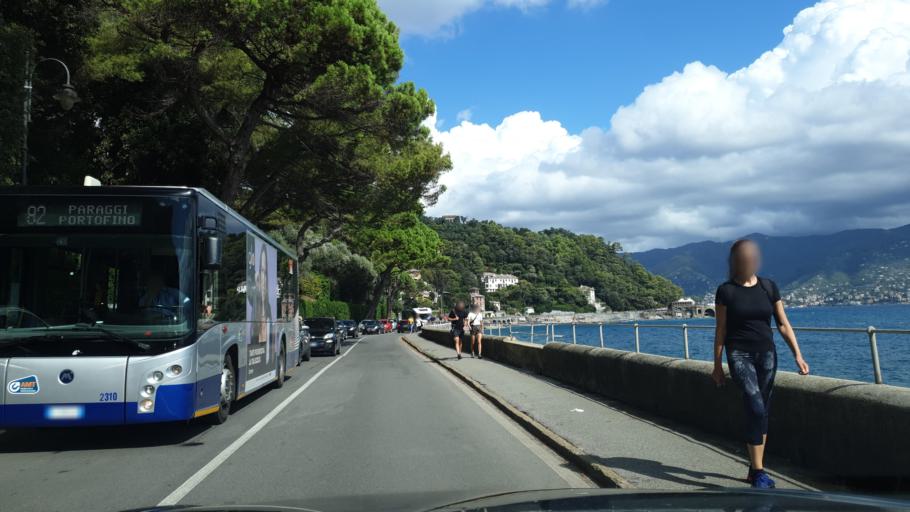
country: IT
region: Liguria
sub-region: Provincia di Genova
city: Portofino
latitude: 44.3162
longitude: 9.2115
